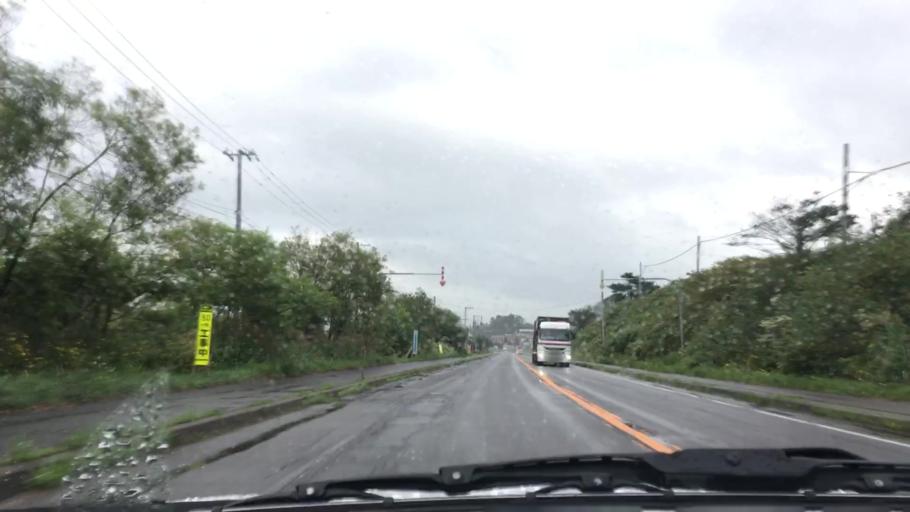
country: JP
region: Hokkaido
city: Nanae
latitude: 42.2388
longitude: 140.3030
